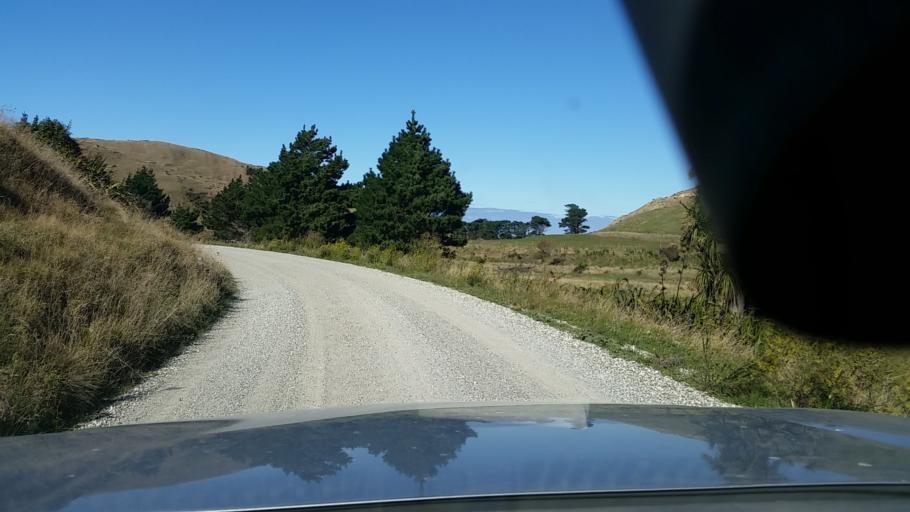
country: NZ
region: Marlborough
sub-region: Marlborough District
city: Blenheim
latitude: -41.8365
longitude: 174.1767
